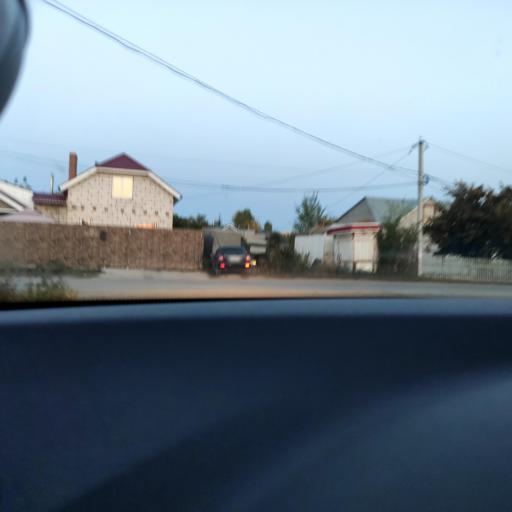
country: RU
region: Samara
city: Novosemeykino
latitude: 53.3688
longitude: 50.3531
